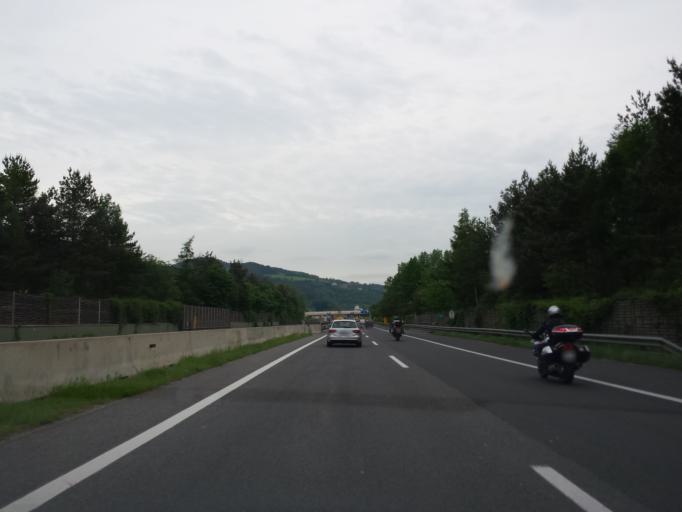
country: AT
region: Lower Austria
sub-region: Politischer Bezirk Neunkirchen
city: Warth
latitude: 47.6373
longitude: 16.1265
